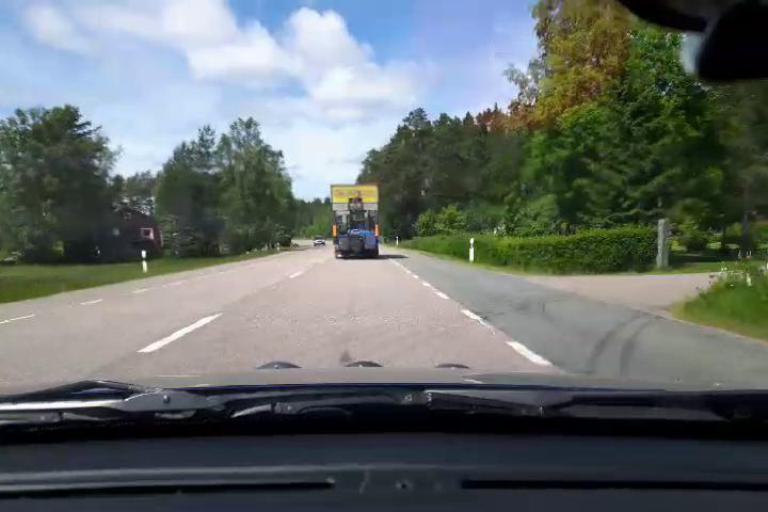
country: SE
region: Uppsala
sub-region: Osthammars Kommun
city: Bjorklinge
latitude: 60.1043
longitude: 17.5489
